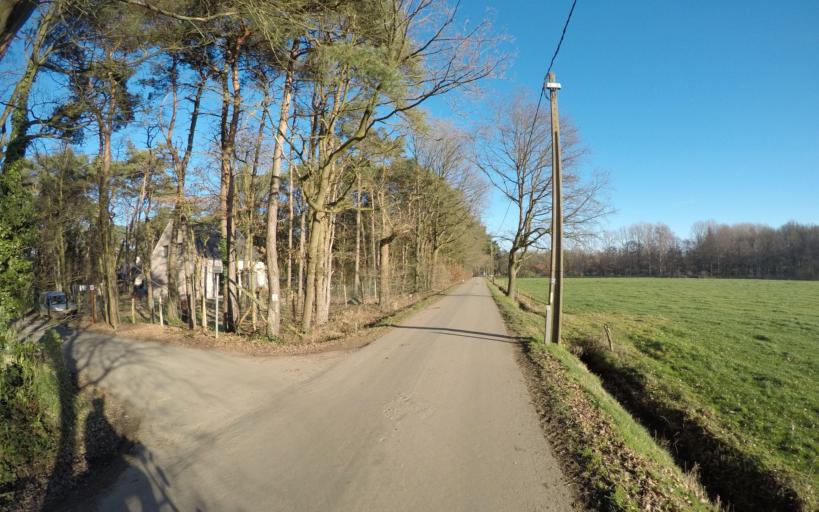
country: BE
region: Flanders
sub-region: Provincie Antwerpen
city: Schilde
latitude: 51.2299
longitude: 4.6094
